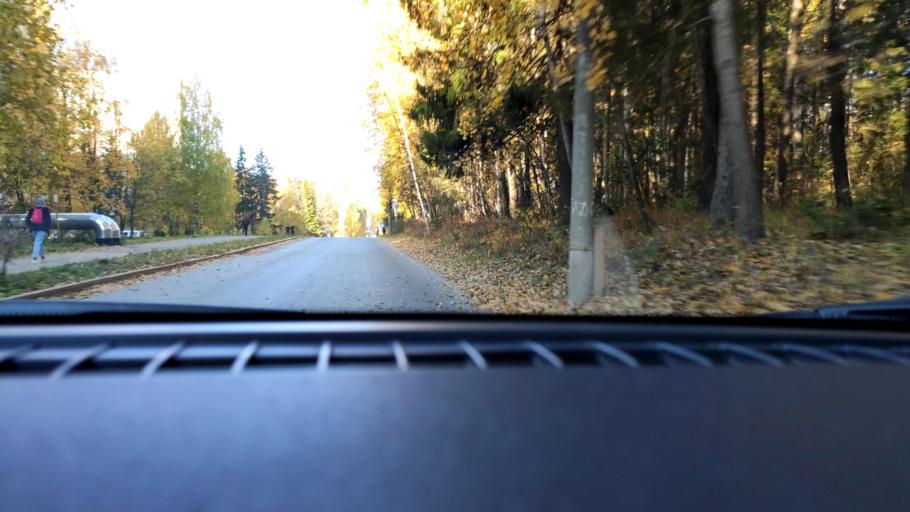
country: RU
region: Perm
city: Perm
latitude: 58.0558
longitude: 56.2184
